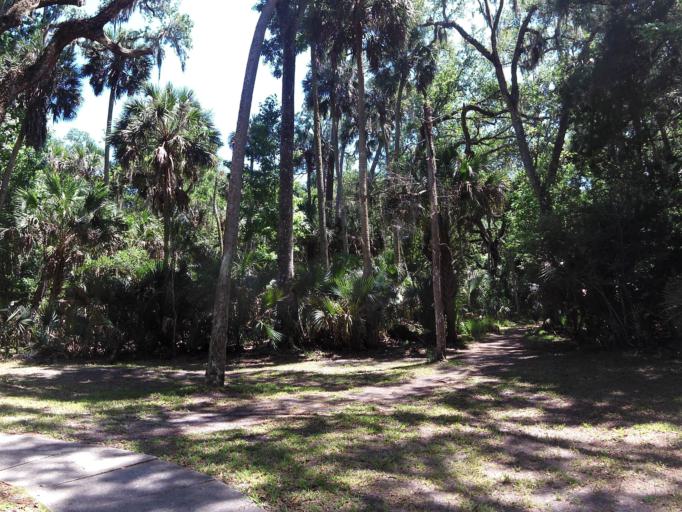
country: US
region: Florida
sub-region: Flagler County
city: Flagler Beach
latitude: 29.4354
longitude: -81.1435
